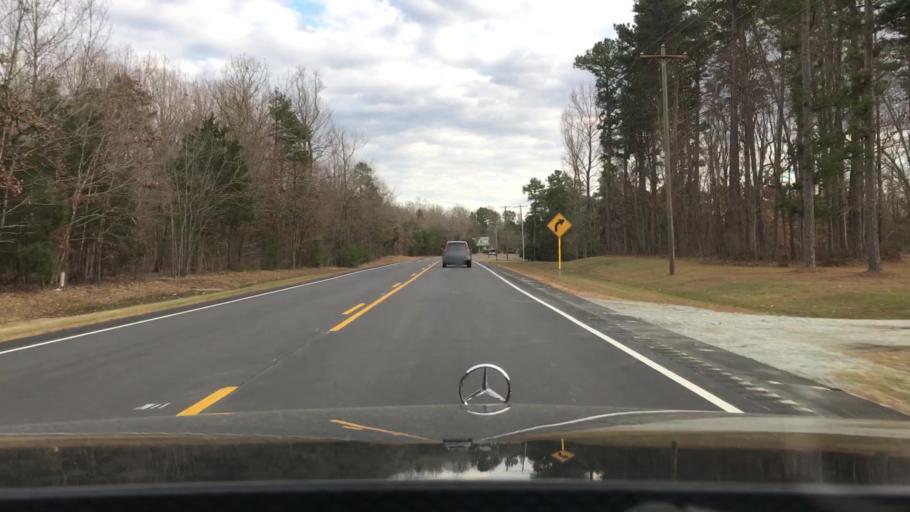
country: US
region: North Carolina
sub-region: Alamance County
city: Mebane
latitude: 36.2722
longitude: -79.2011
